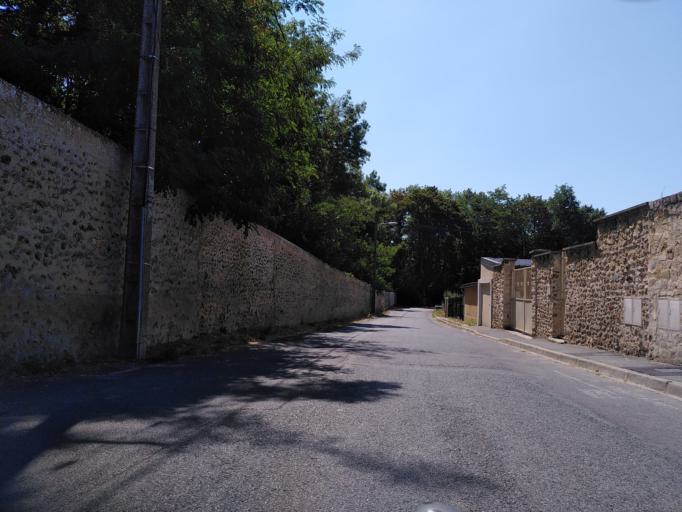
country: FR
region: Ile-de-France
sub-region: Departement de l'Essonne
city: Arpajon
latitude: 48.5907
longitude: 2.2334
